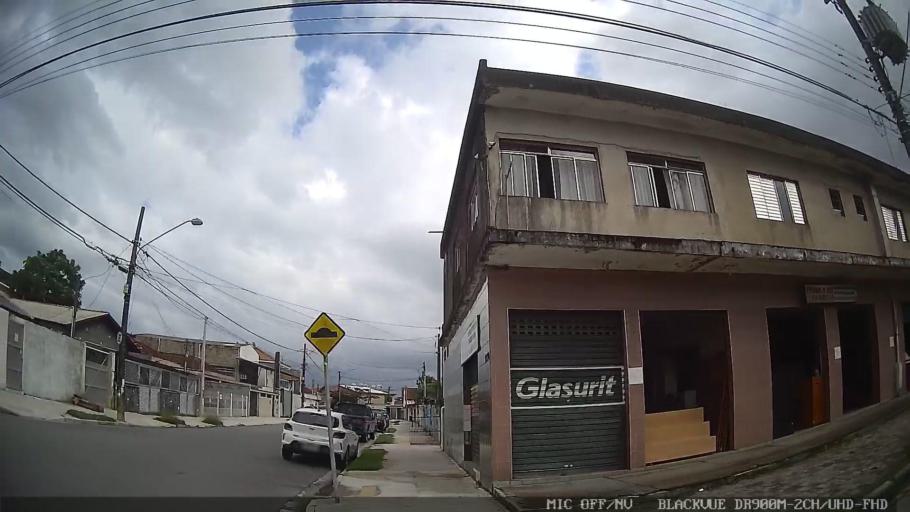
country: BR
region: Sao Paulo
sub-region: Guaruja
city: Guaruja
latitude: -23.9912
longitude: -46.2841
